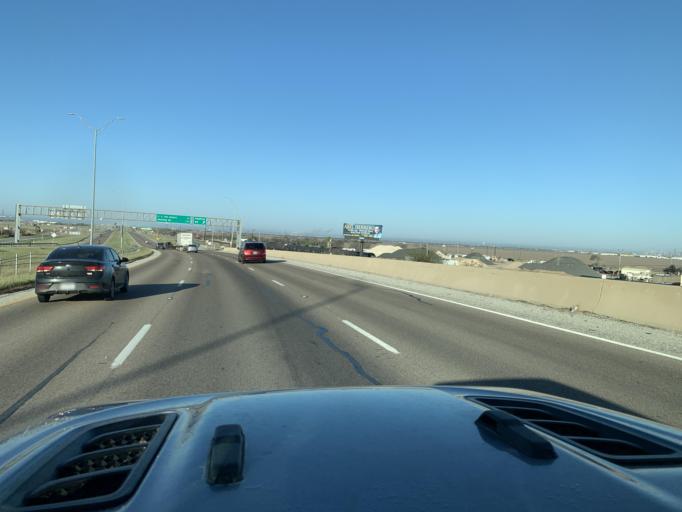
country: US
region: Texas
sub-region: Nueces County
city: Corpus Christi
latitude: 27.7850
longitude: -97.4878
